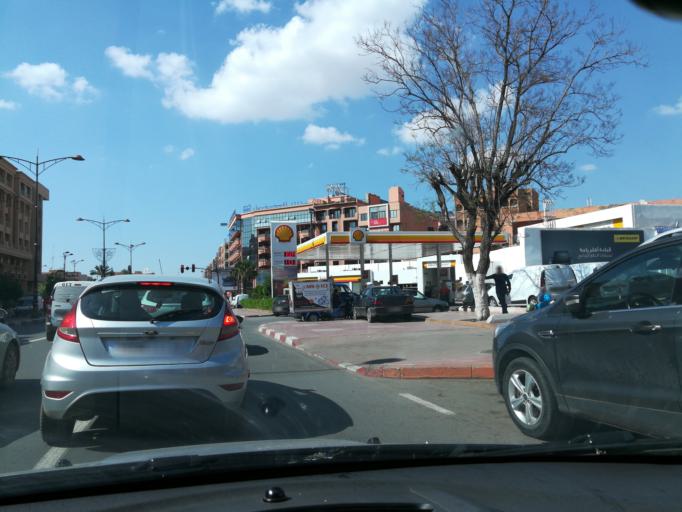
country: MA
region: Marrakech-Tensift-Al Haouz
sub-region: Marrakech
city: Marrakesh
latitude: 31.6368
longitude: -8.0175
